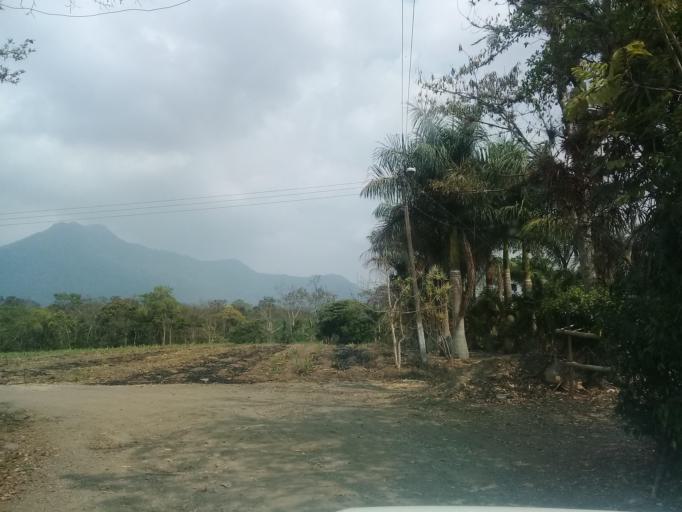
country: MX
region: Veracruz
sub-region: Ixtaczoquitlan
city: Capoluca
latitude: 18.8200
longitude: -96.9911
